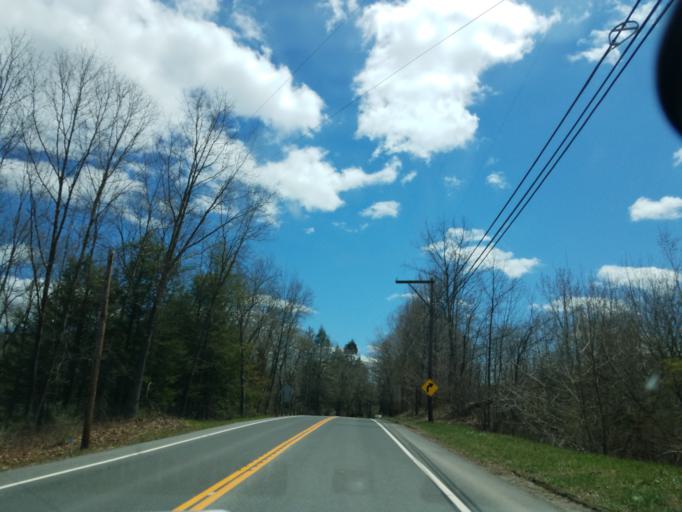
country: US
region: Connecticut
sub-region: Fairfield County
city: Sherman
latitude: 41.6252
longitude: -73.4662
